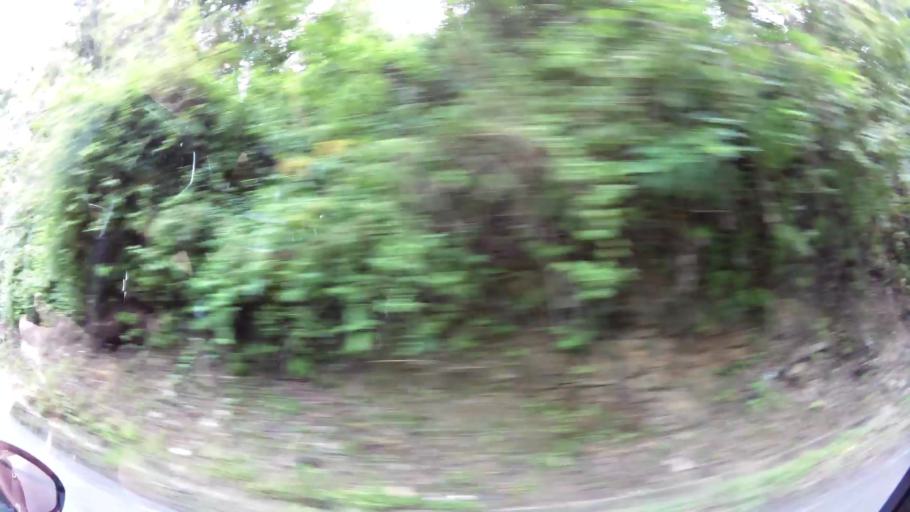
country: TT
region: Diego Martin
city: Petit Valley
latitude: 10.7349
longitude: -61.4928
